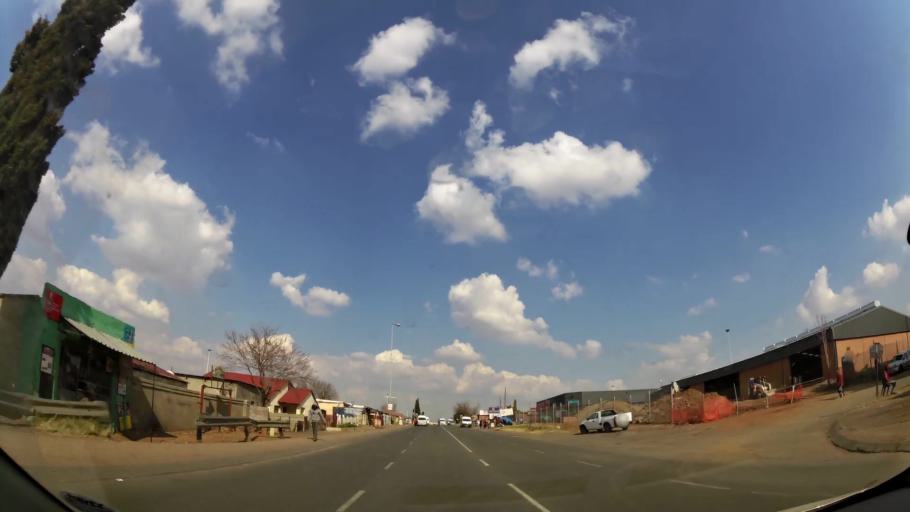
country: ZA
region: Gauteng
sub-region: Ekurhuleni Metropolitan Municipality
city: Germiston
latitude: -26.3151
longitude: 28.1573
